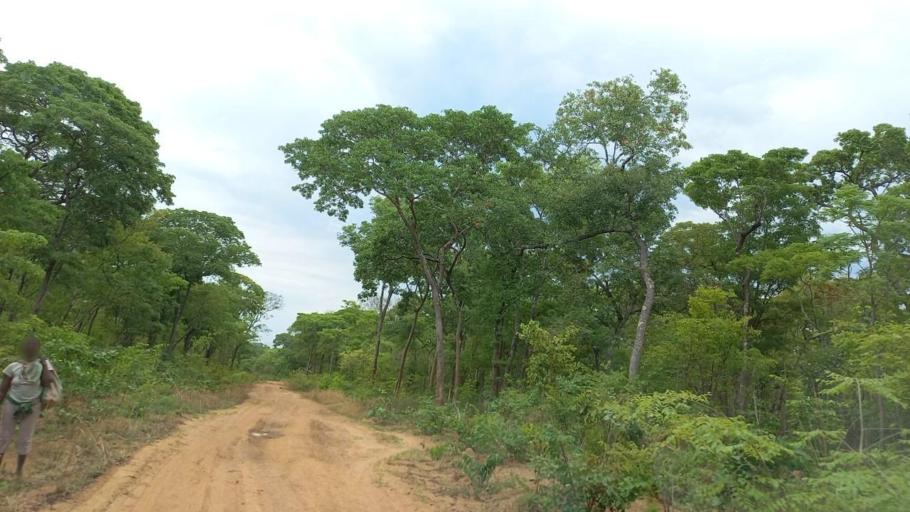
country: ZM
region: North-Western
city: Kalengwa
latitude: -13.5408
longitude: 24.9778
